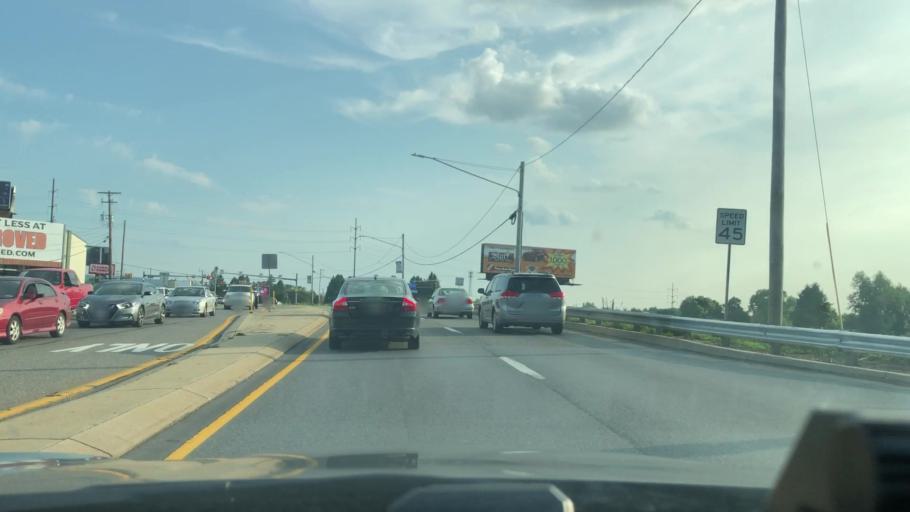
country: US
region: Pennsylvania
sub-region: Lehigh County
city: Fullerton
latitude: 40.6333
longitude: -75.4407
